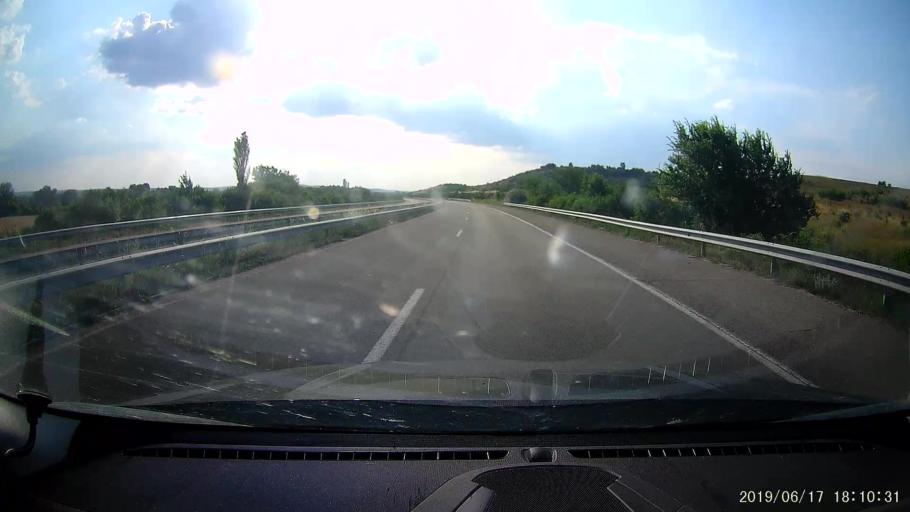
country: BG
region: Khaskovo
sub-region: Obshtina Lyubimets
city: Lyubimets
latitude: 41.8753
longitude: 26.0755
